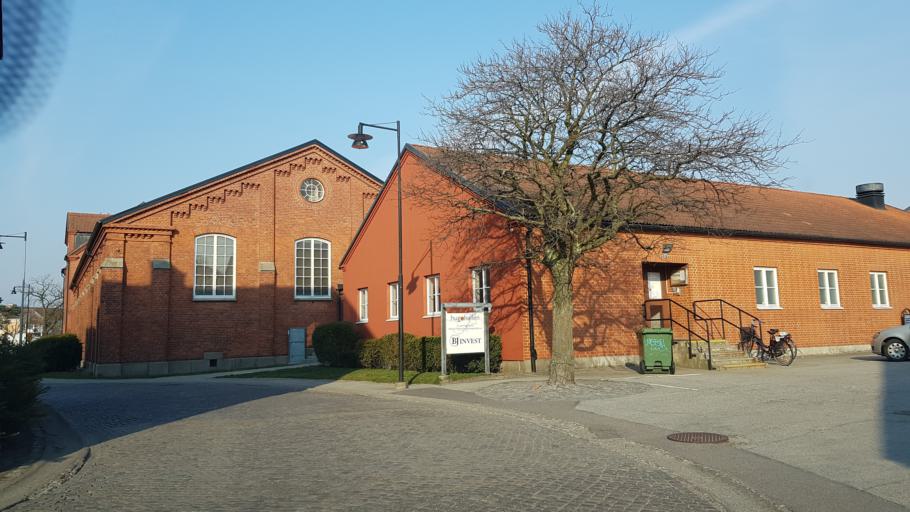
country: SE
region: Skane
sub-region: Ystads Kommun
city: Ystad
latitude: 55.4328
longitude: 13.8413
